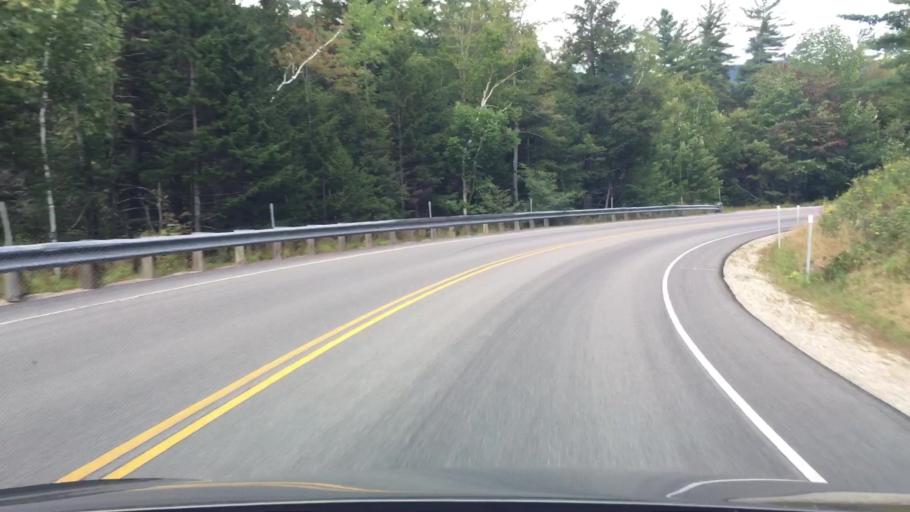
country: US
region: New Hampshire
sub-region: Carroll County
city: North Conway
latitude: 44.0125
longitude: -71.2624
